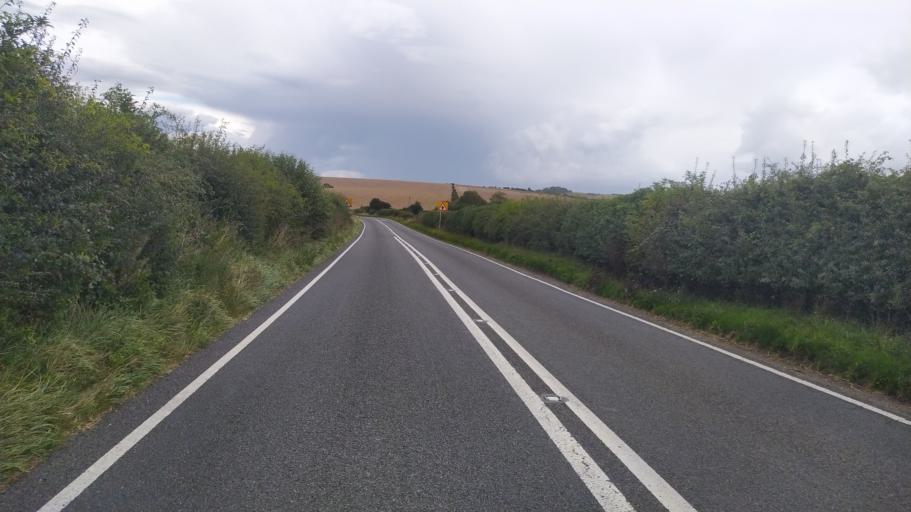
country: GB
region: England
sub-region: Wiltshire
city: Bower Chalke
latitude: 50.9375
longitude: -2.0024
